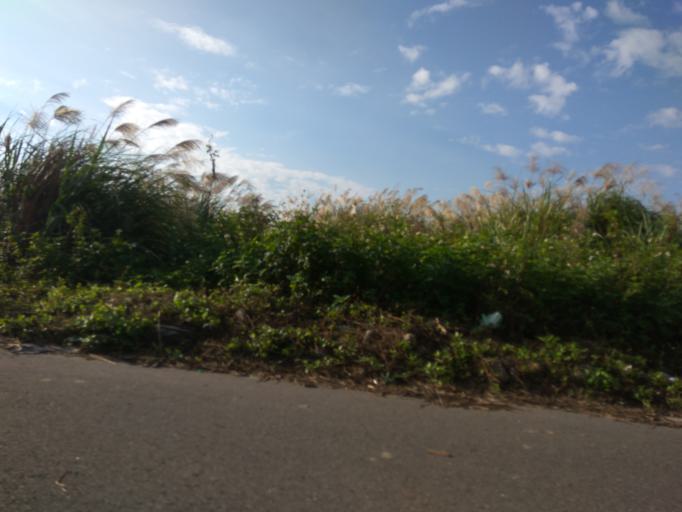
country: TW
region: Taiwan
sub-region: Hsinchu
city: Zhubei
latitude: 24.9804
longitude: 121.0548
